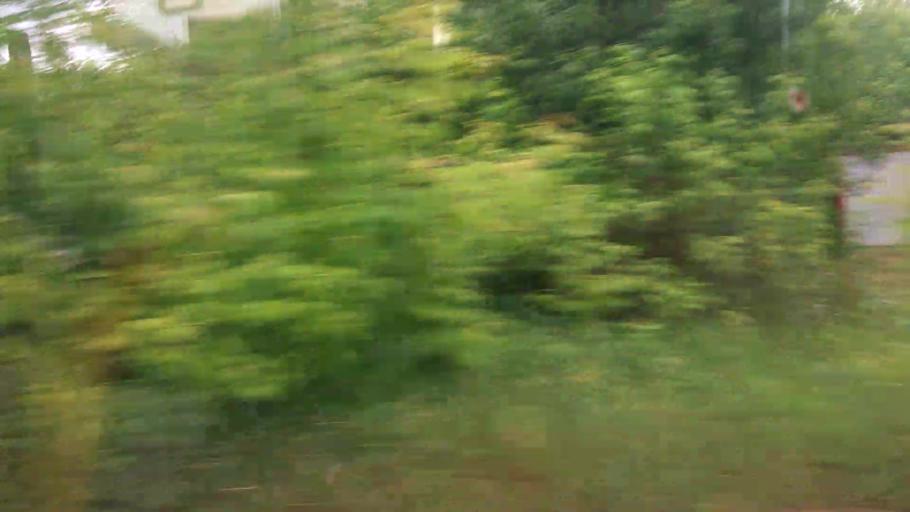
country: RU
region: Moskovskaya
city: Ozery
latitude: 54.8514
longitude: 38.5700
